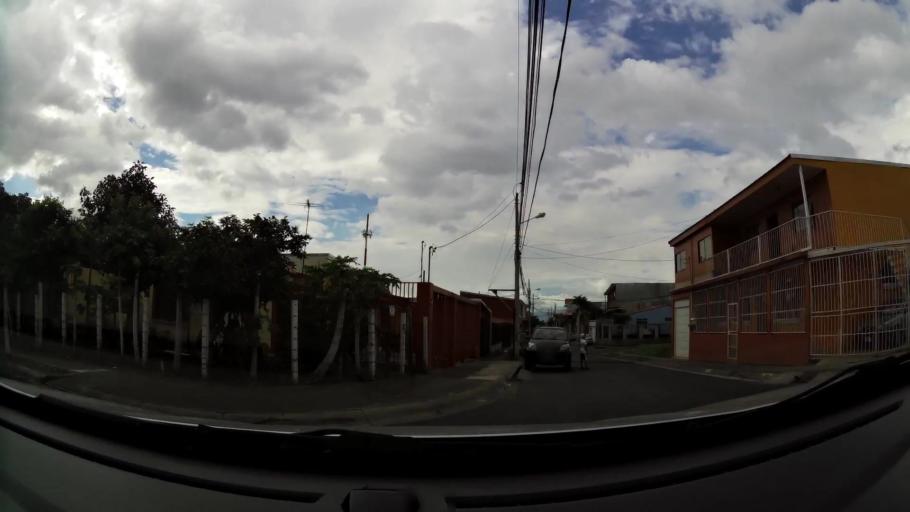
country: CR
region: San Jose
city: San Felipe
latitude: 9.9154
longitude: -84.1177
